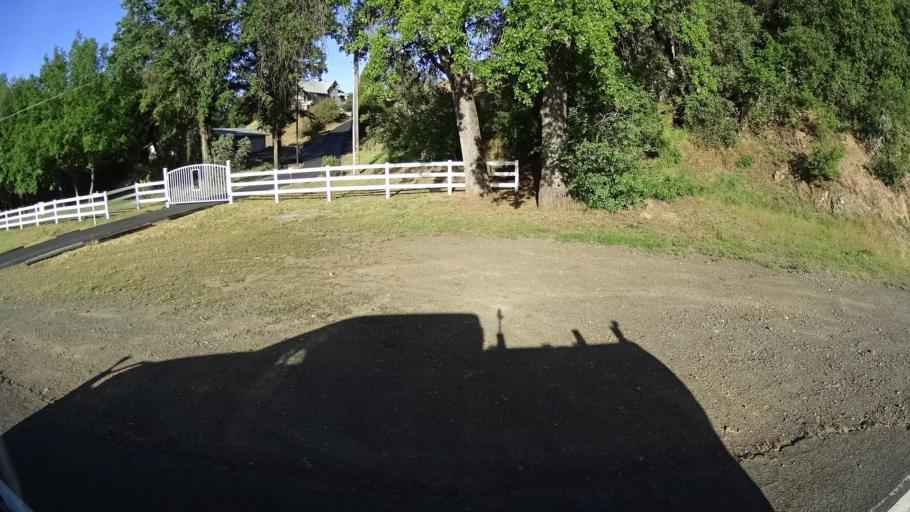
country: US
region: California
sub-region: Lake County
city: North Lakeport
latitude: 39.0908
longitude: -122.9498
